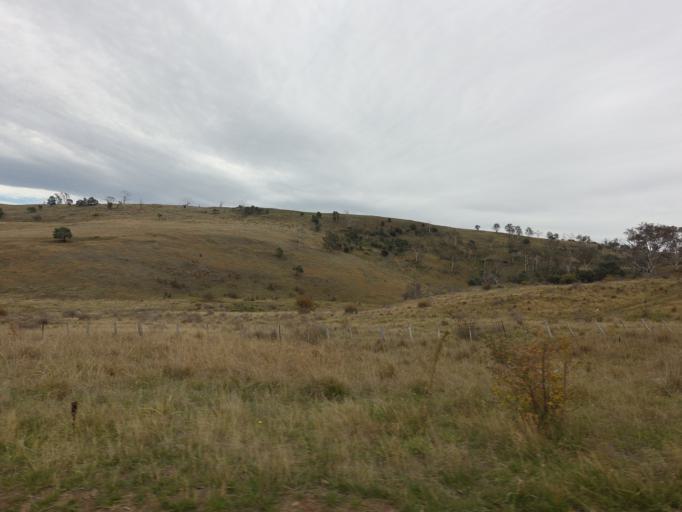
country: AU
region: Tasmania
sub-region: Derwent Valley
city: New Norfolk
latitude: -42.3634
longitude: 146.8427
